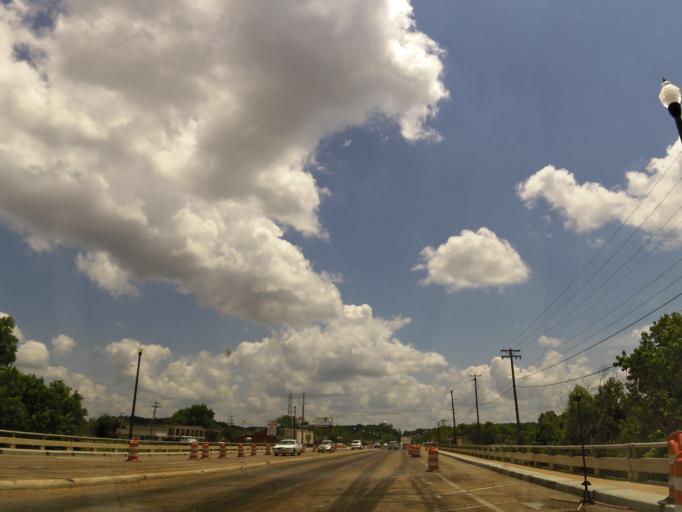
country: US
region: Mississippi
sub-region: Lee County
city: Tupelo
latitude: 34.2576
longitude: -88.6924
